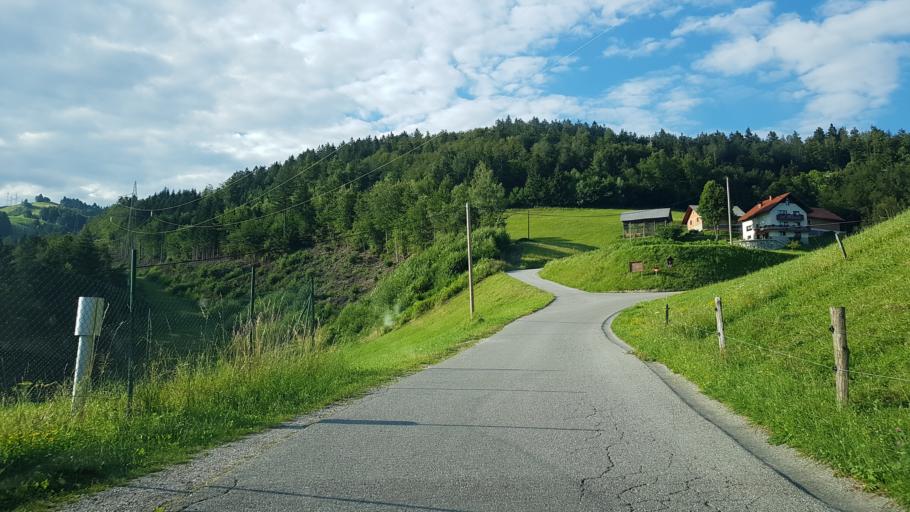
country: SI
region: Idrija
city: Spodnja Idrija
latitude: 46.0726
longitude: 14.0147
